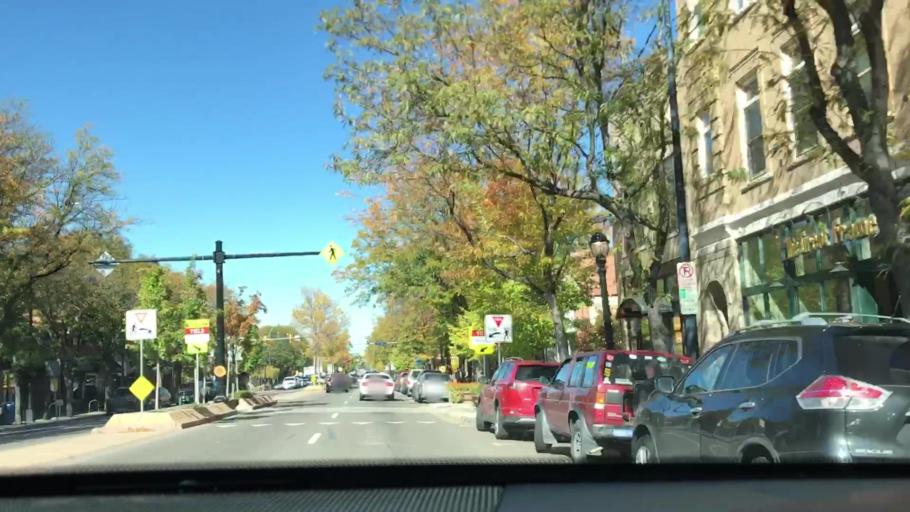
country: US
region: Colorado
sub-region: Boulder County
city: Longmont
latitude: 40.1663
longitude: -105.1024
